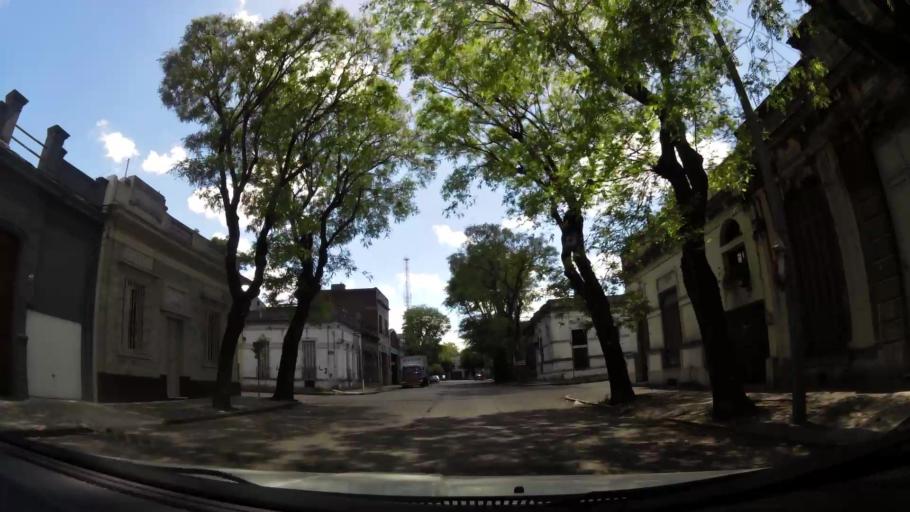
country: UY
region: Montevideo
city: Montevideo
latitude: -34.8827
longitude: -56.1884
